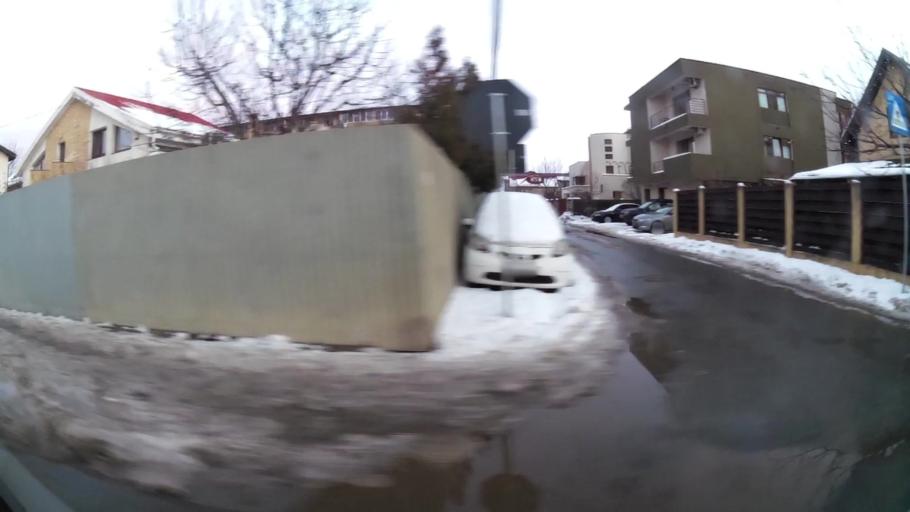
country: RO
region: Ilfov
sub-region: Comuna Popesti-Leordeni
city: Popesti-Leordeni
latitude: 44.3737
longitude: 26.1553
